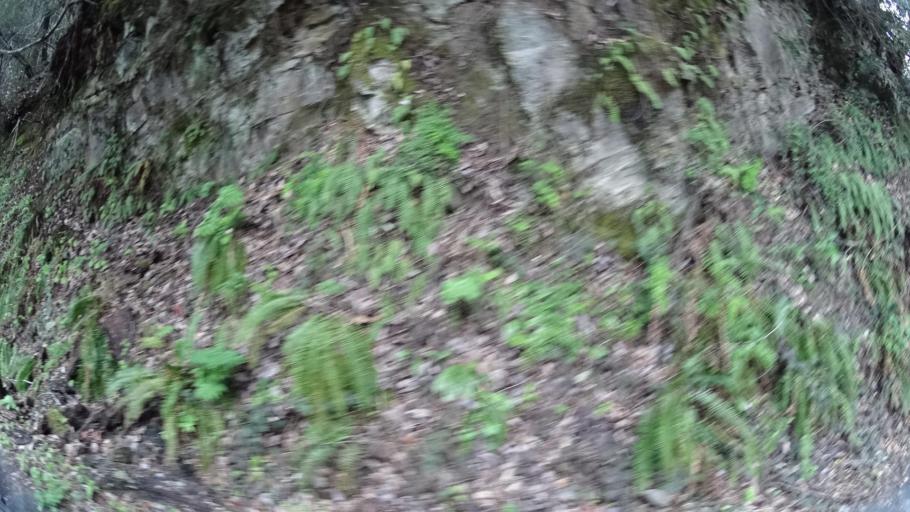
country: US
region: California
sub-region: Humboldt County
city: Blue Lake
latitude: 40.8756
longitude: -123.8826
